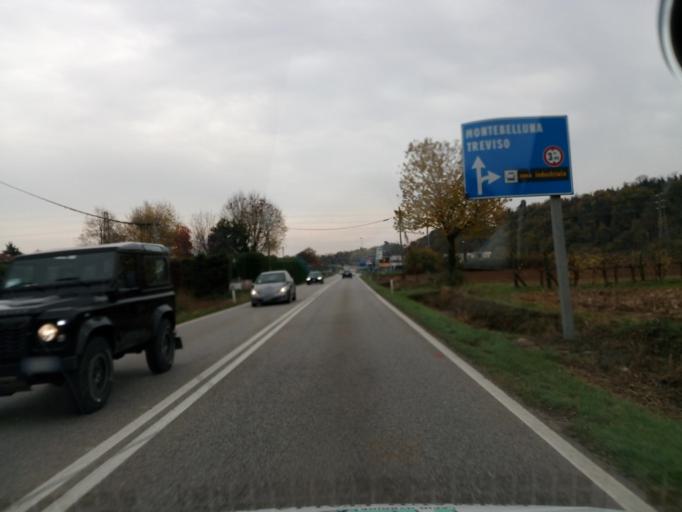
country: IT
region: Veneto
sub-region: Provincia di Treviso
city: Montebelluna
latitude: 45.7885
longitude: 12.0457
